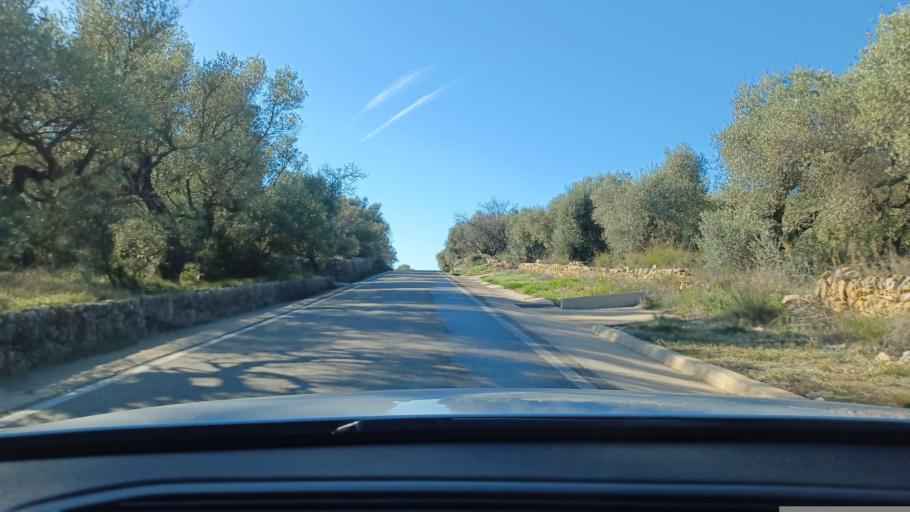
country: ES
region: Valencia
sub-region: Provincia de Castello
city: Rosell
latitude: 40.6360
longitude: 0.2987
